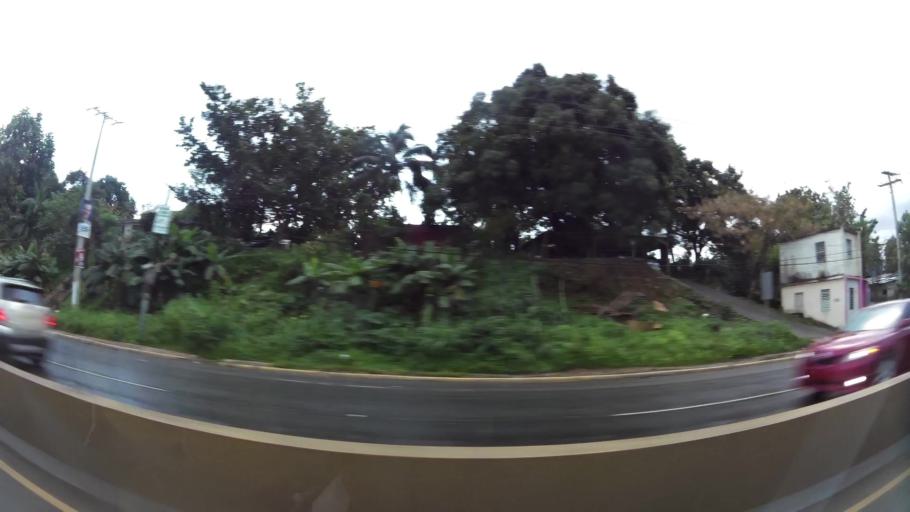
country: DO
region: Santo Domingo
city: Santo Domingo Oeste
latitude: 18.5671
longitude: -70.0883
